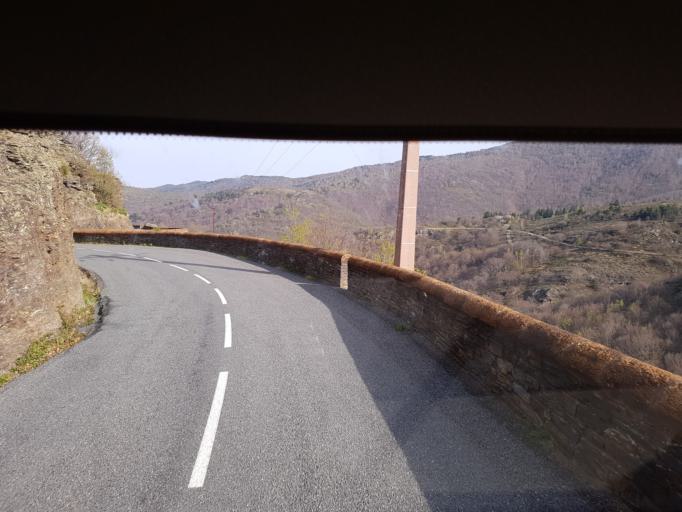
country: FR
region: Languedoc-Roussillon
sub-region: Departement du Gard
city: Branoux-les-Taillades
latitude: 44.3270
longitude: 3.8491
